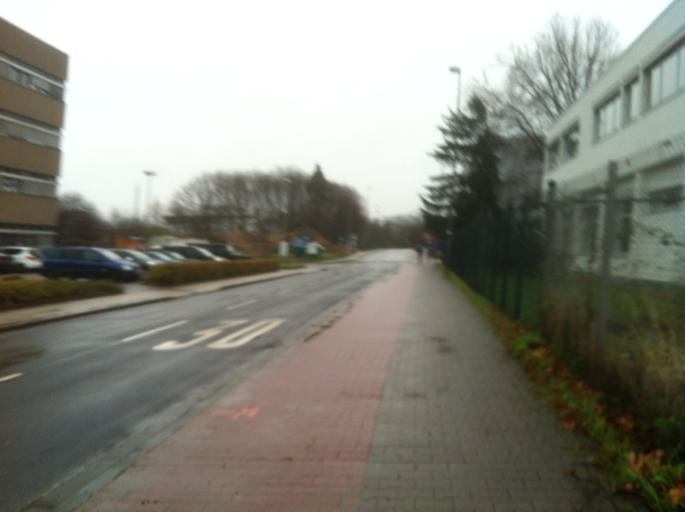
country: DE
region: Rheinland-Pfalz
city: Mainz
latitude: 49.9894
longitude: 8.2351
